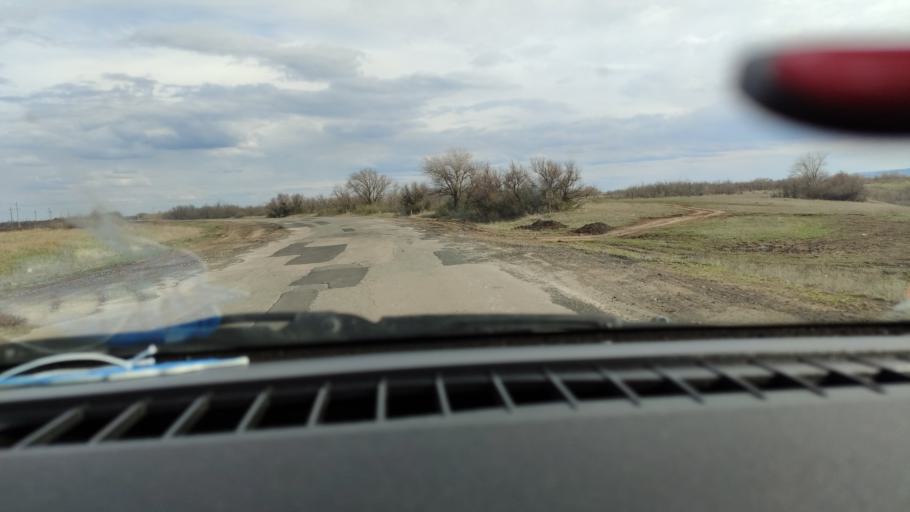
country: RU
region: Saratov
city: Rovnoye
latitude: 51.0540
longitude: 46.0358
